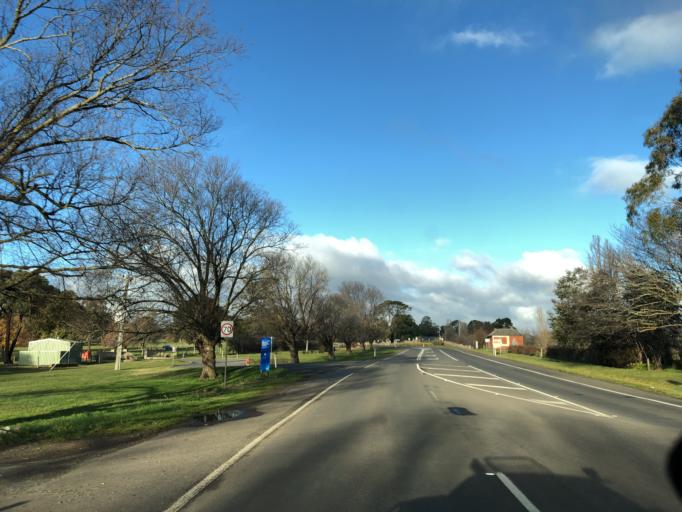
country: AU
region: Victoria
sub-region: Mount Alexander
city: Castlemaine
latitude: -37.1897
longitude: 144.3910
